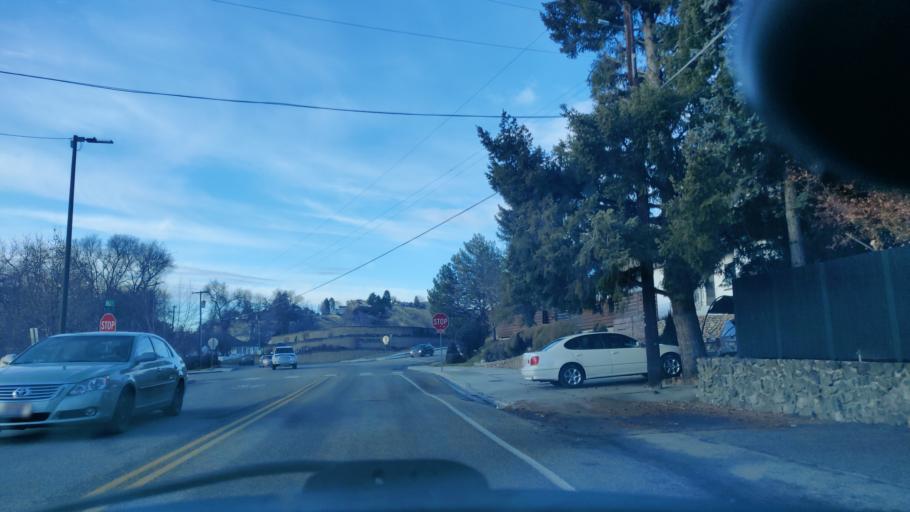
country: US
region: Idaho
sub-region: Ada County
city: Boise
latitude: 43.6386
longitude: -116.2054
